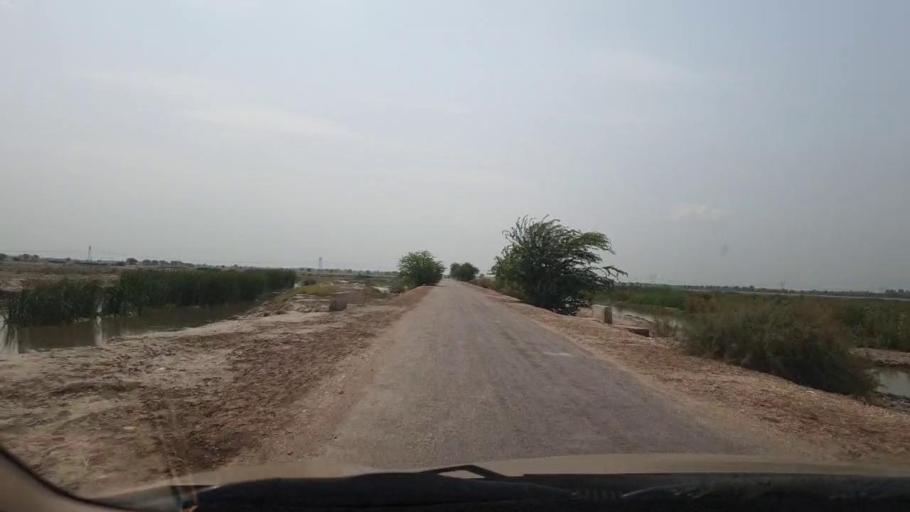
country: PK
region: Sindh
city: Goth Garelo
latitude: 27.5004
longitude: 68.1156
